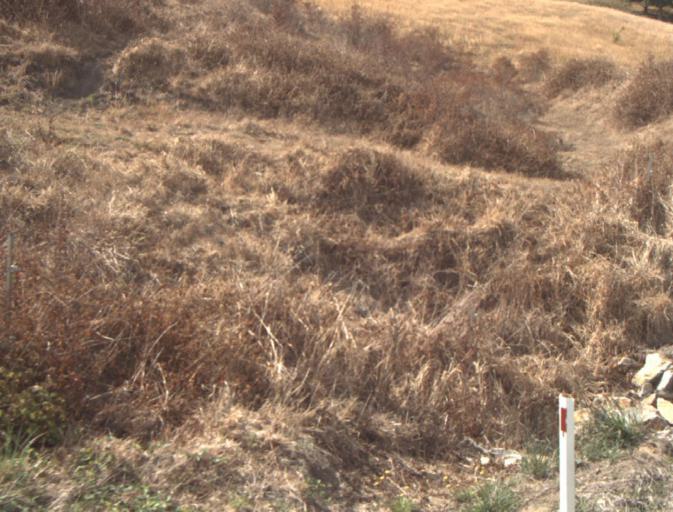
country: AU
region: Tasmania
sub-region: Launceston
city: Mayfield
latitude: -41.2417
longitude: 147.1496
